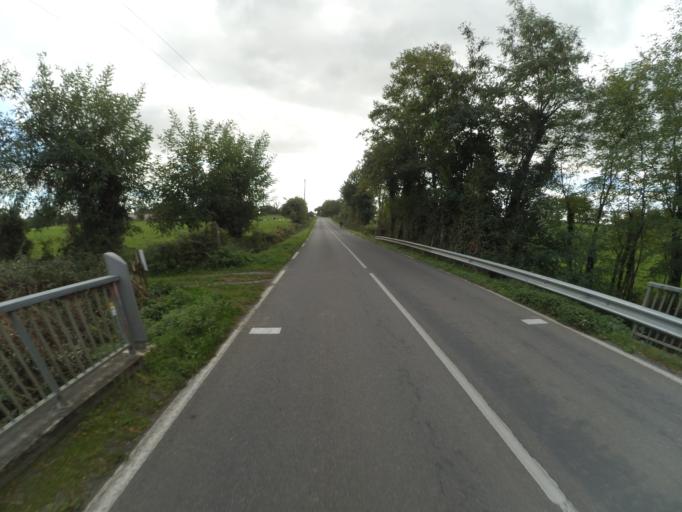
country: FR
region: Pays de la Loire
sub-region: Departement de la Loire-Atlantique
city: Suce-sur-Erdre
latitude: 47.3228
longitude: -1.5116
